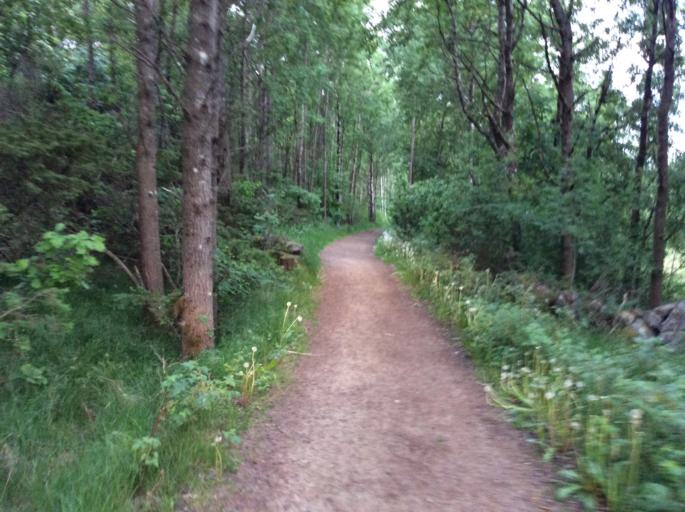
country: SE
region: Vaestra Goetaland
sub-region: Goteborg
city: Majorna
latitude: 57.8009
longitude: 11.8826
